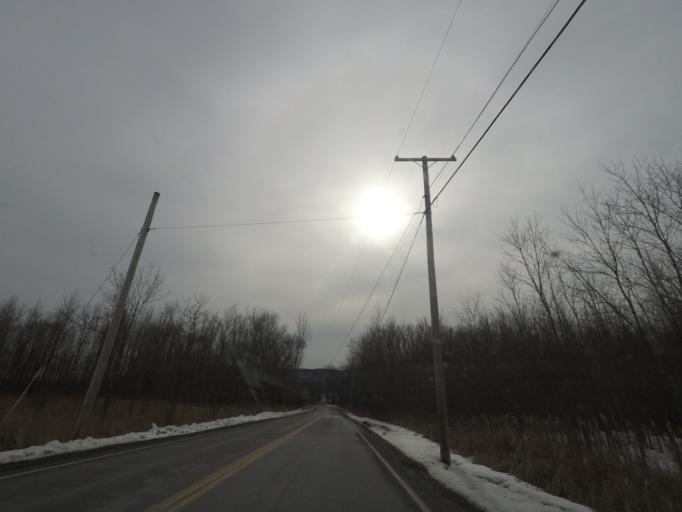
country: US
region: New York
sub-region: Albany County
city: Voorheesville
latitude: 42.6725
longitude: -73.9827
